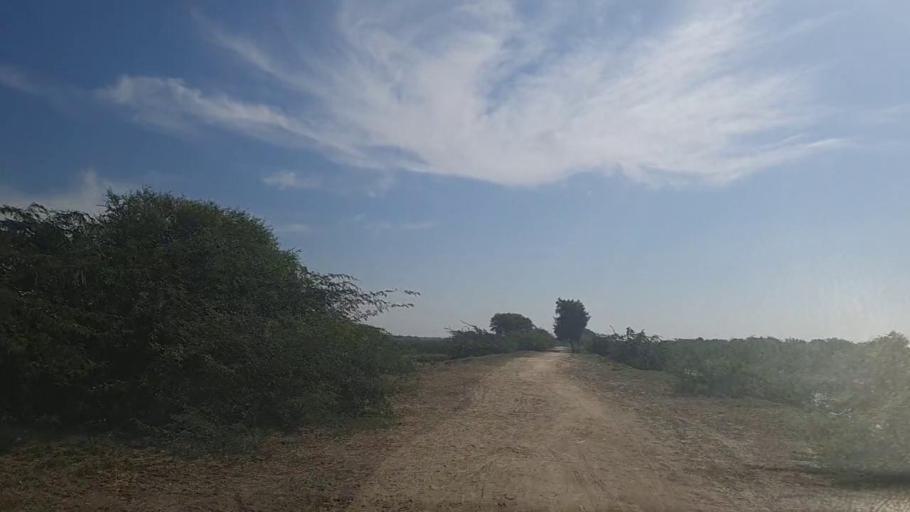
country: PK
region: Sindh
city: Mirpur Batoro
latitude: 24.6618
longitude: 68.1911
